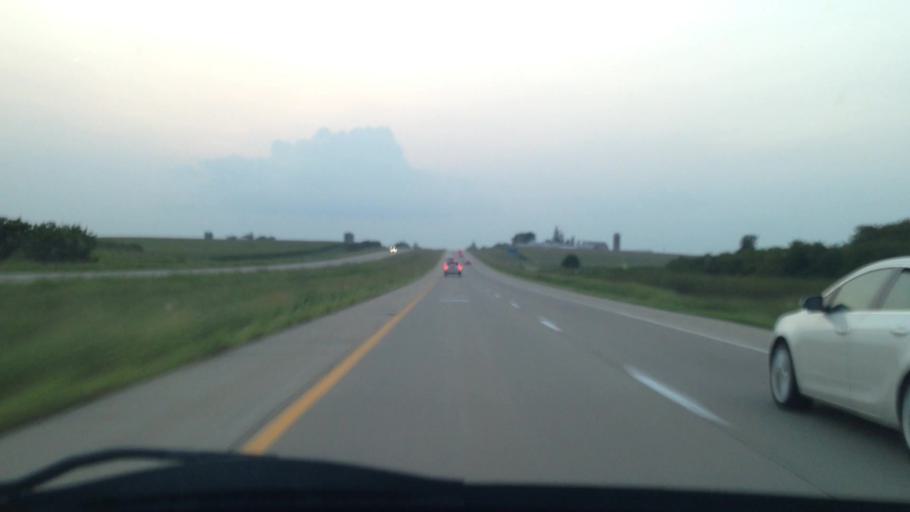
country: US
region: Iowa
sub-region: Black Hawk County
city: La Porte City
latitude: 42.3936
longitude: -92.1399
